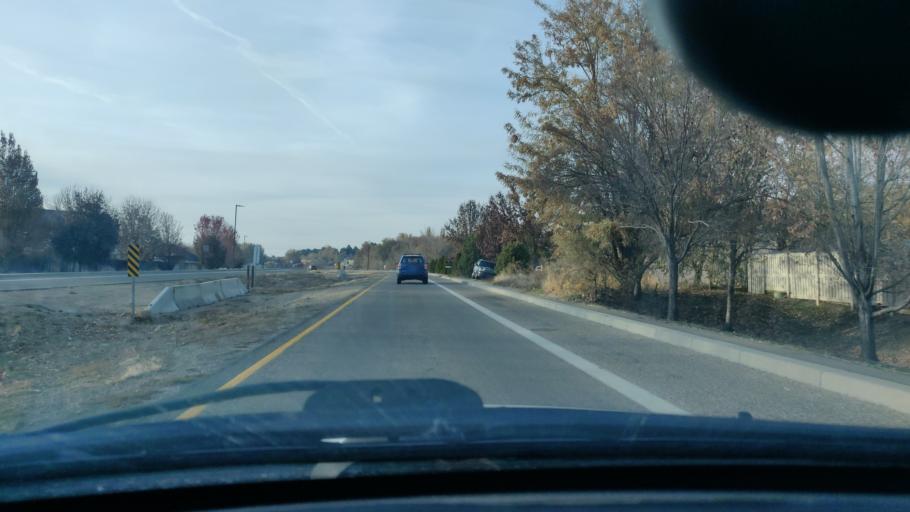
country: US
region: Idaho
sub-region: Ada County
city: Eagle
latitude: 43.6852
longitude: -116.2917
